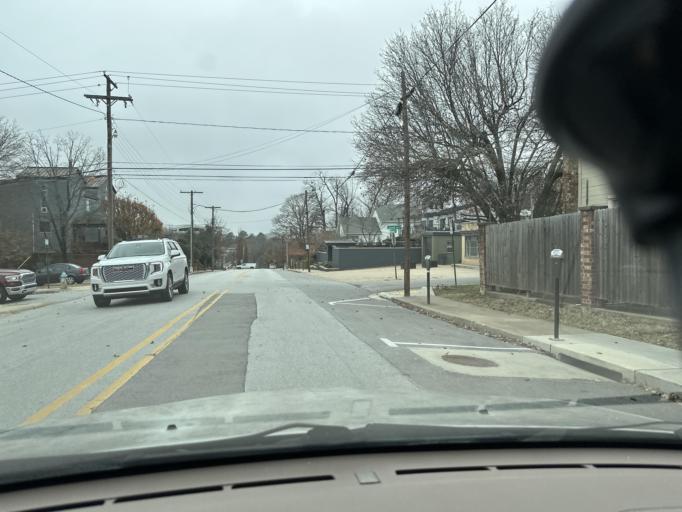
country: US
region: Arkansas
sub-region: Washington County
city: Fayetteville
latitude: 36.0620
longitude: -94.1629
